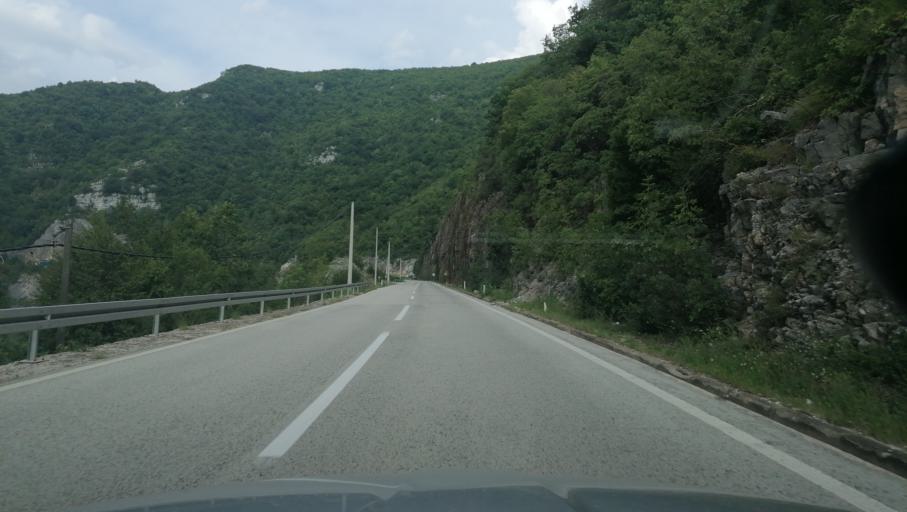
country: BA
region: Republika Srpska
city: Mrkonjic Grad
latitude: 44.4649
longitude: 17.2043
